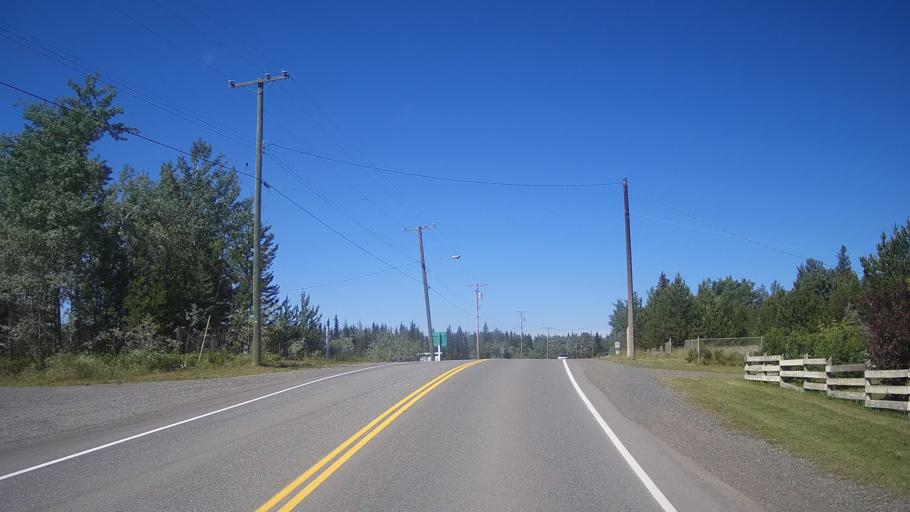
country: CA
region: British Columbia
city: Cache Creek
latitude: 51.5547
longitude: -121.2086
